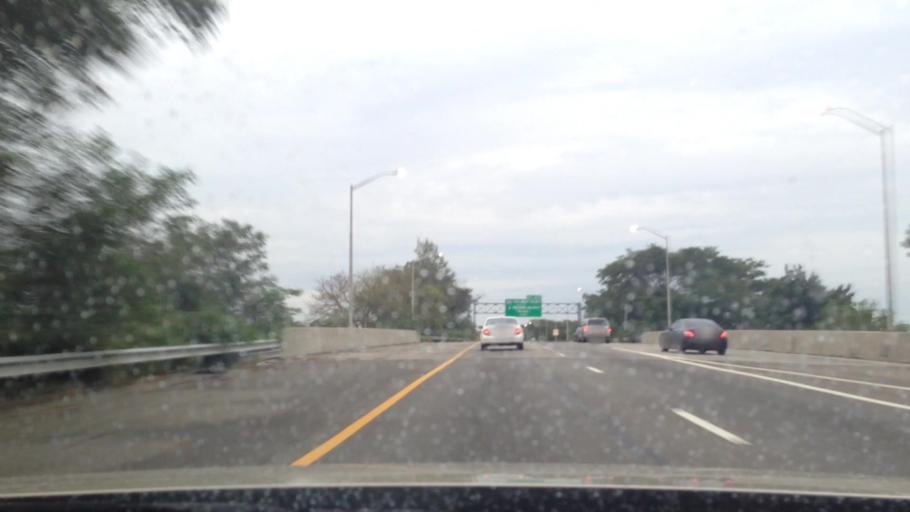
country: US
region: New York
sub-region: Queens County
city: Borough of Queens
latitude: 40.6640
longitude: -73.8237
